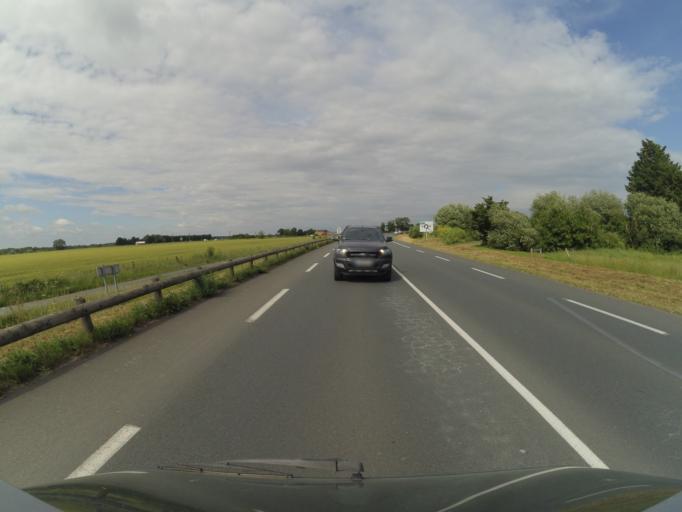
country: FR
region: Pays de la Loire
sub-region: Departement de la Vendee
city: Champagne-les-Marais
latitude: 46.4256
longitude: -1.0937
